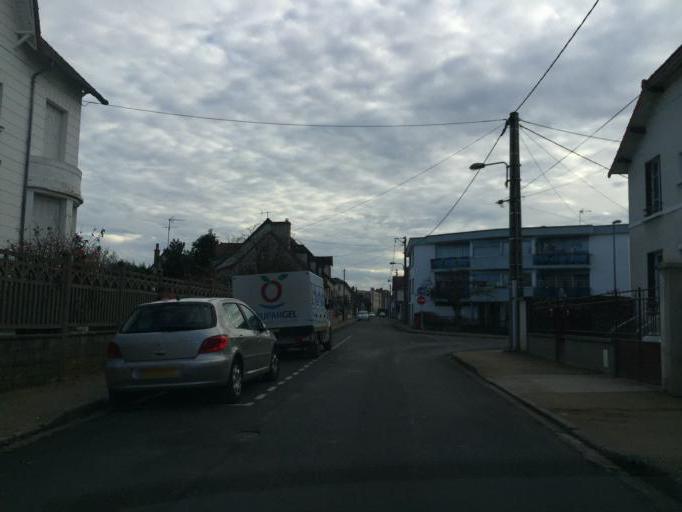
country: FR
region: Auvergne
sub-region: Departement de l'Allier
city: Moulins
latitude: 46.5730
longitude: 3.3367
